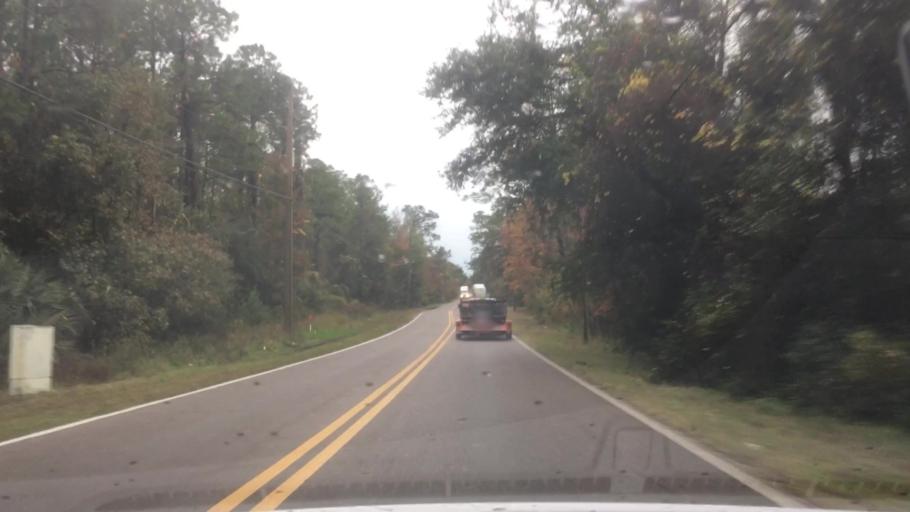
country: US
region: Florida
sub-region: Duval County
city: Jacksonville
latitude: 30.4258
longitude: -81.5629
